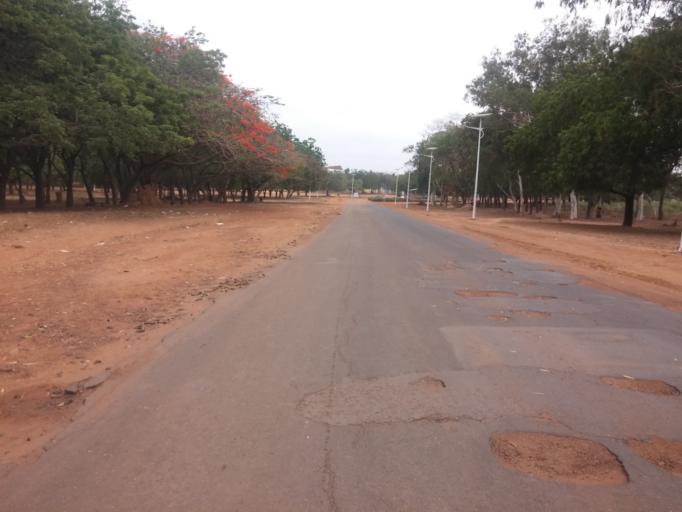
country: TG
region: Maritime
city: Lome
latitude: 6.1729
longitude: 1.2172
